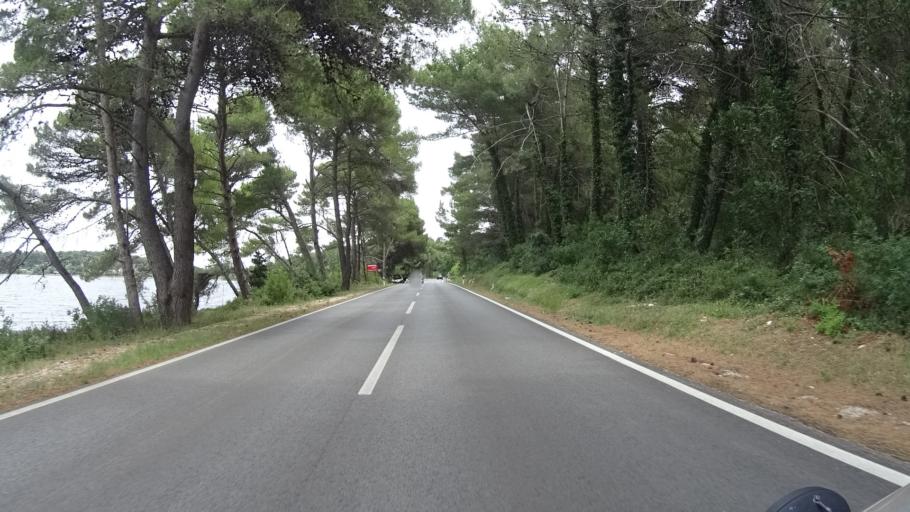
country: HR
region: Istarska
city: Medulin
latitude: 44.8168
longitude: 13.8887
